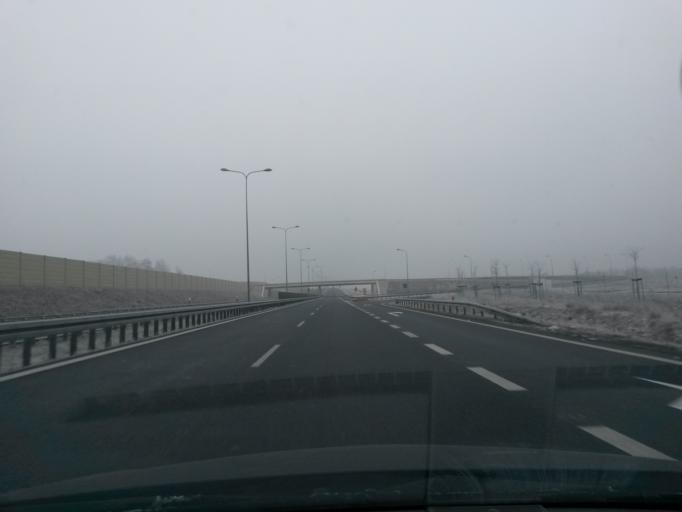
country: PL
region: Greater Poland Voivodeship
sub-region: Powiat gnieznienski
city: Lubowo
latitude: 52.4857
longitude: 17.4262
